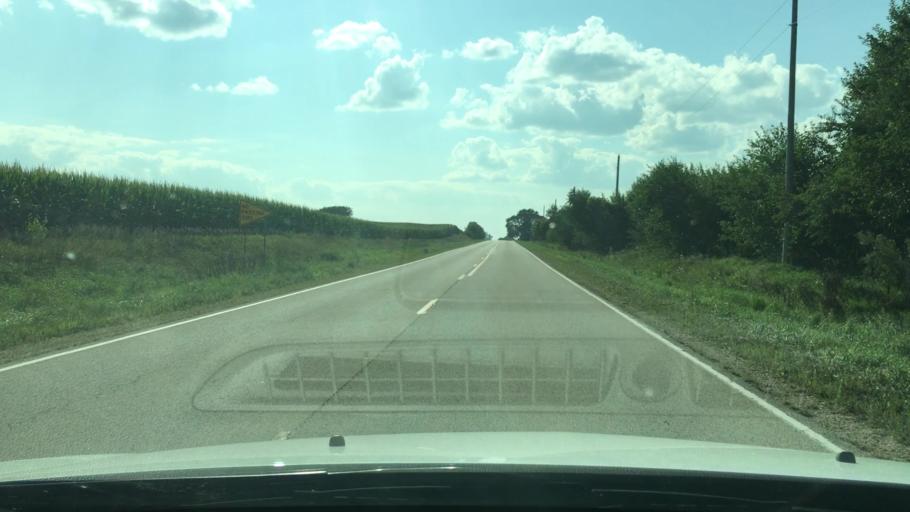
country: US
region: Illinois
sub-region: Ogle County
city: Rochelle
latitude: 41.8484
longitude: -88.9770
